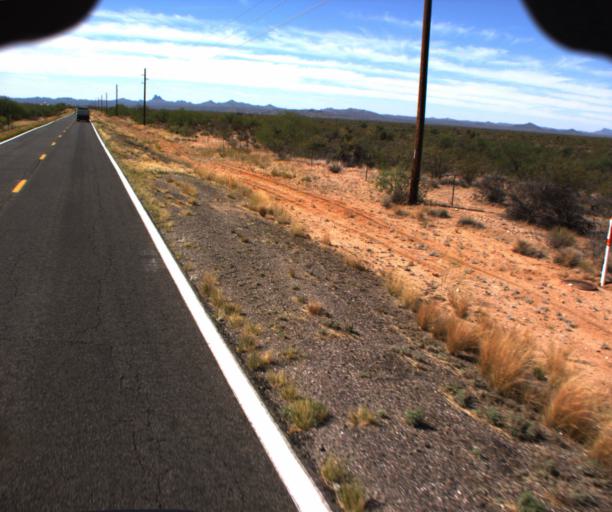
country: US
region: Arizona
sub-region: Yavapai County
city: Congress
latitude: 34.0929
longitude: -112.8280
